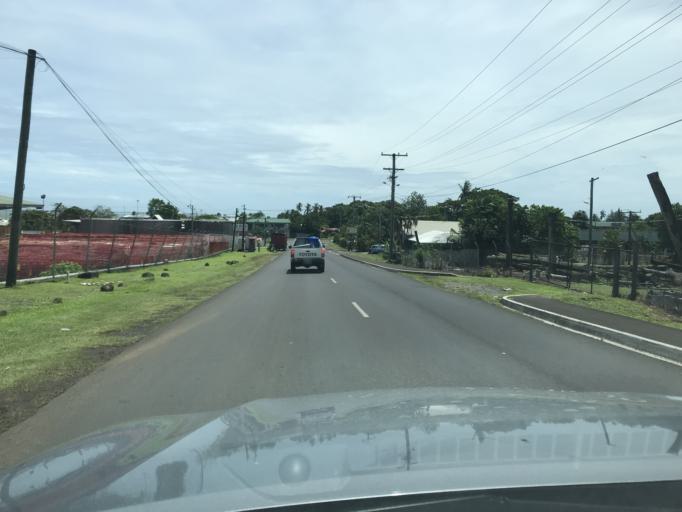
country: WS
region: Tuamasaga
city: Vaiusu
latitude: -13.8240
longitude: -171.8013
